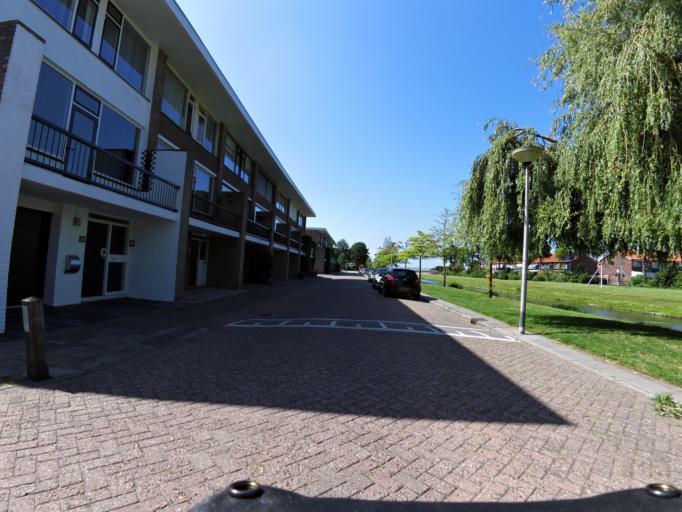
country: NL
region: South Holland
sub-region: Gemeente Brielle
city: Brielle
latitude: 51.9007
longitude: 4.1516
